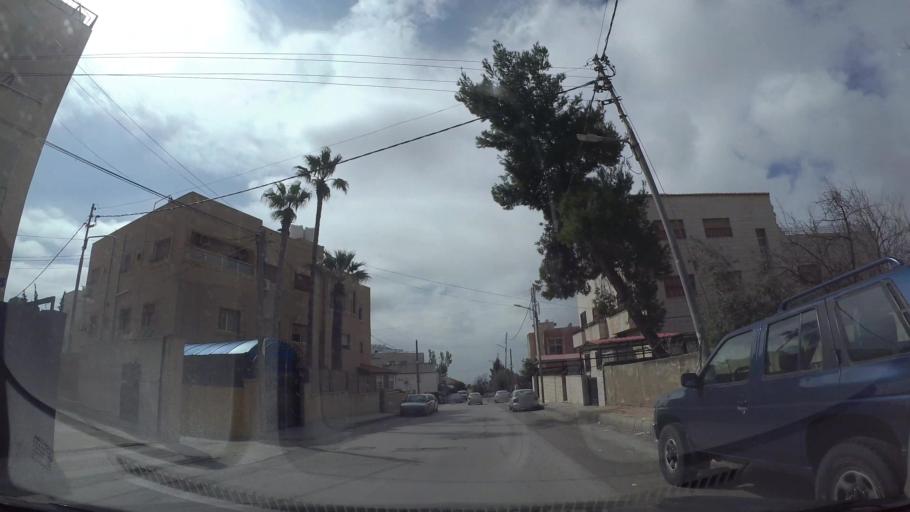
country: JO
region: Amman
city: Wadi as Sir
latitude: 31.9501
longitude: 35.8279
